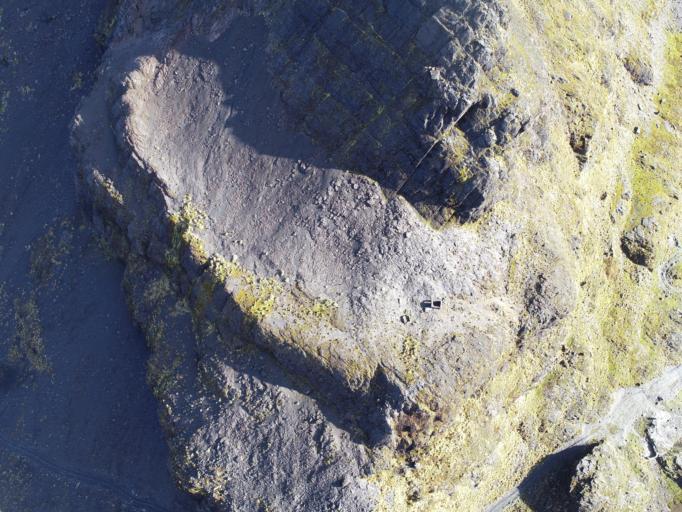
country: PE
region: Puno
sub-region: San Antonio De Putina
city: Sina
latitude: -14.7414
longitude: -69.0542
